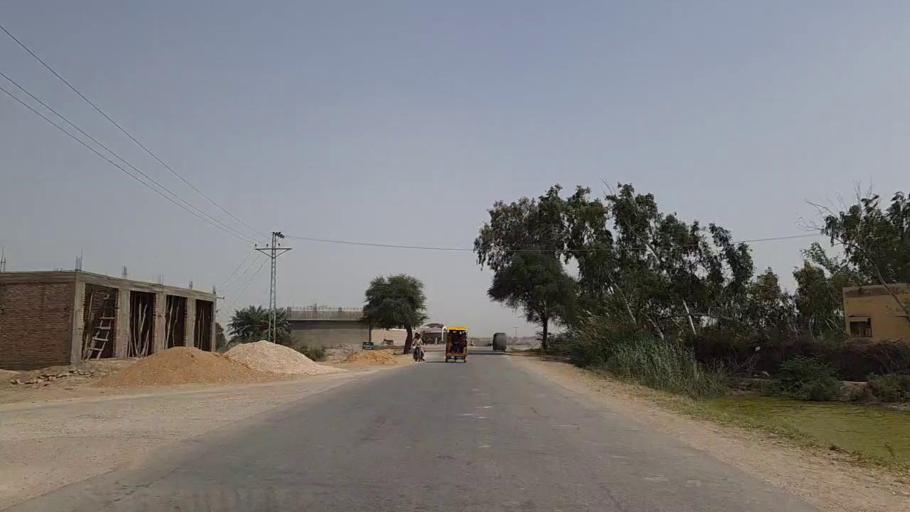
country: PK
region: Sindh
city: Talhar
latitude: 24.8825
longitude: 68.8283
